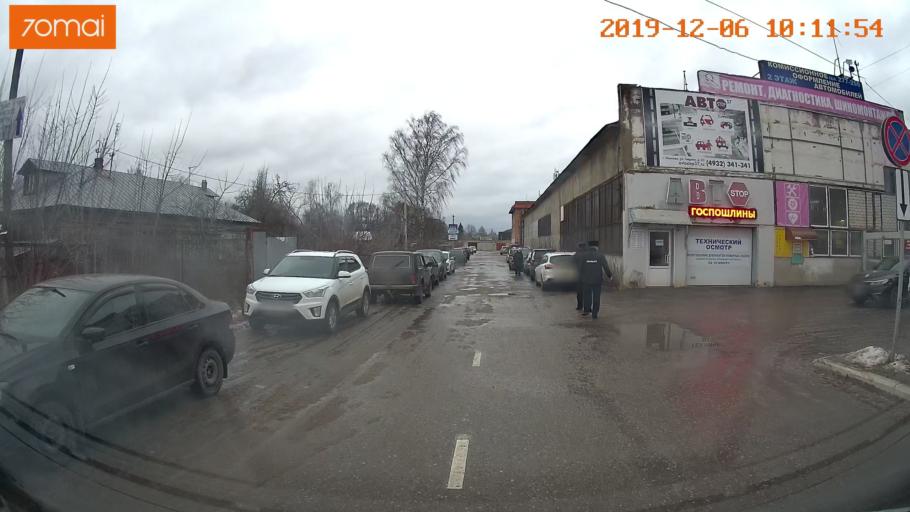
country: RU
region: Ivanovo
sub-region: Gorod Ivanovo
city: Ivanovo
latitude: 57.0318
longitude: 40.9745
